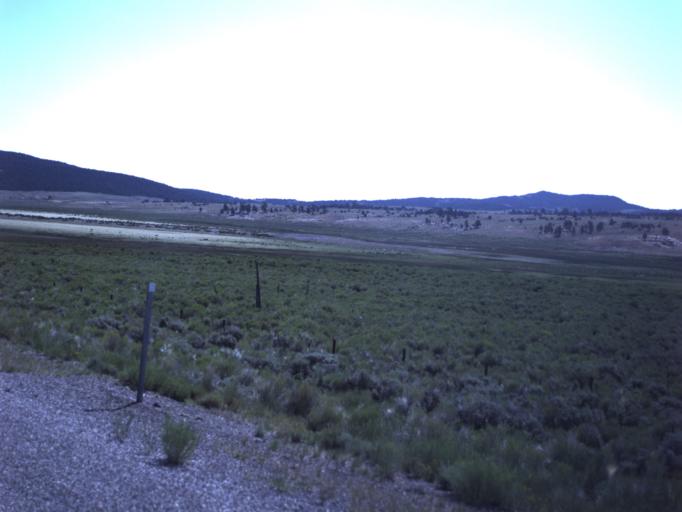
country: US
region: Utah
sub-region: Wayne County
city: Loa
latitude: 38.6265
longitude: -111.4486
